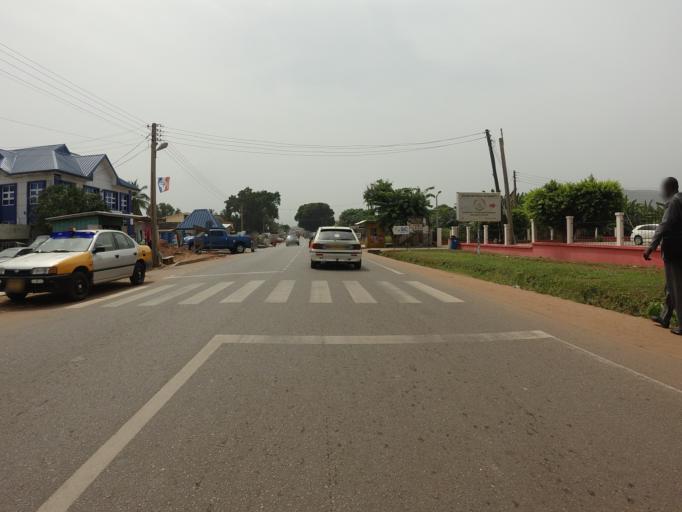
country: GH
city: Akropong
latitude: 6.0992
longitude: -0.0179
